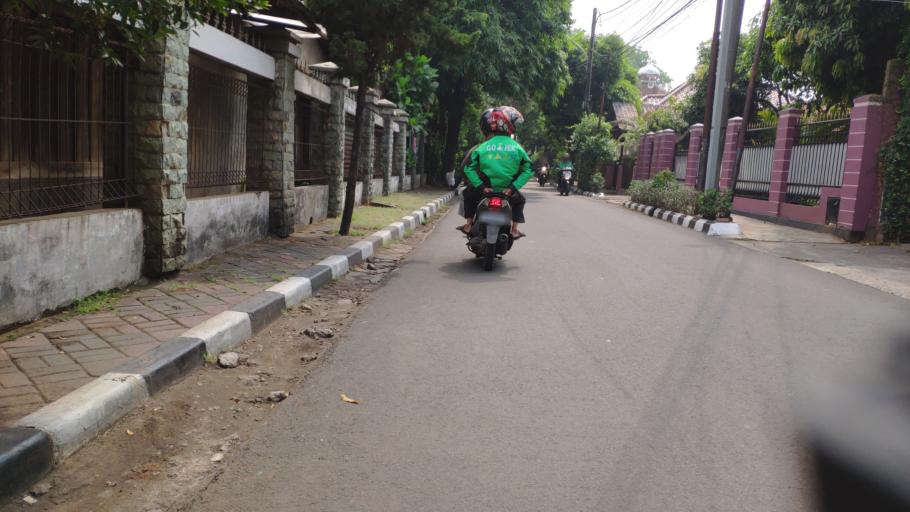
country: ID
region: West Java
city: Pamulang
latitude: -6.3068
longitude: 106.8129
